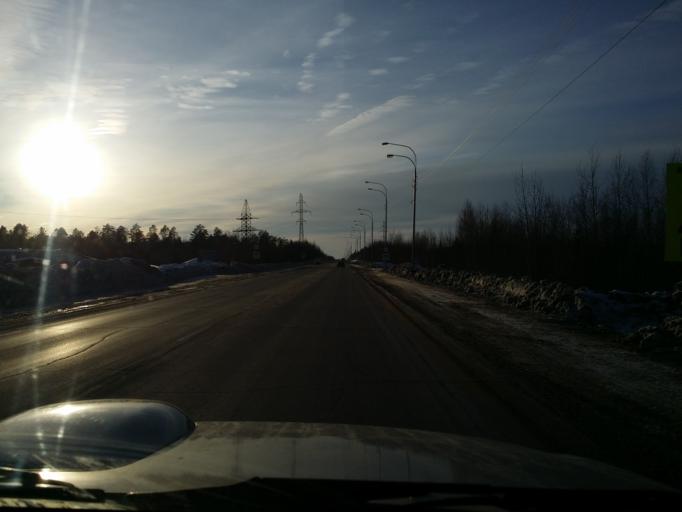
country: RU
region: Khanty-Mansiyskiy Avtonomnyy Okrug
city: Izluchinsk
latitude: 60.9640
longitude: 76.8771
